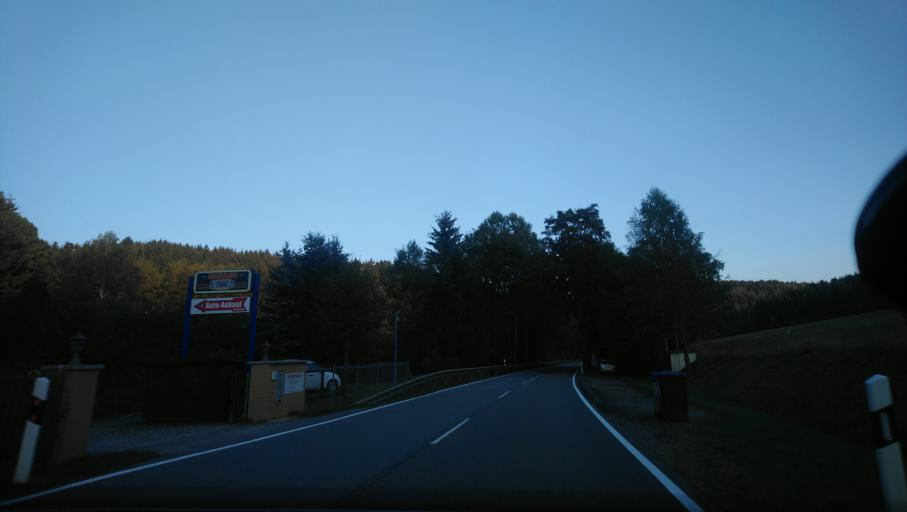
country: DE
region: Saxony
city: Tannenberg
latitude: 50.6068
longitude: 12.9749
